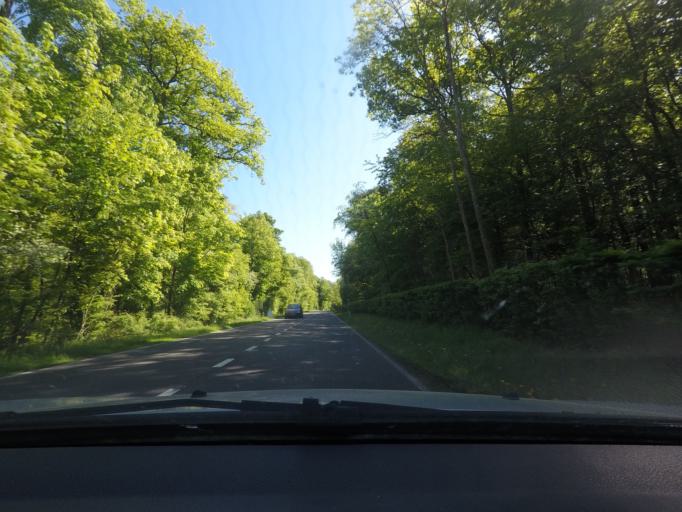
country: BE
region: Wallonia
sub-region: Province du Luxembourg
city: Wellin
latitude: 50.1704
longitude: 5.1095
